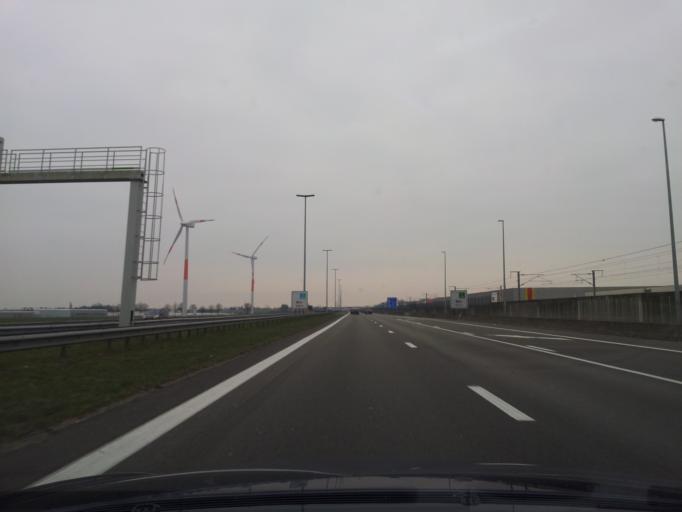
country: NL
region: North Brabant
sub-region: Gemeente Zundert
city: Zundert
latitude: 51.4712
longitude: 4.7280
